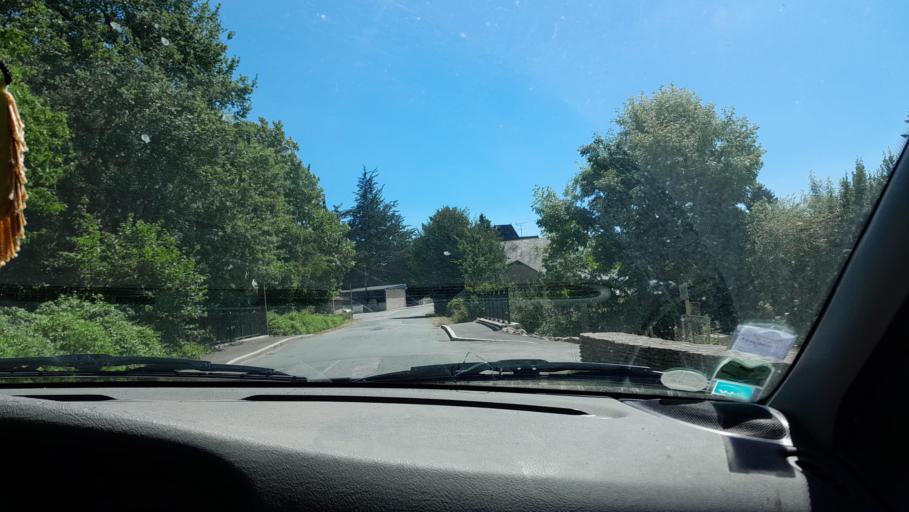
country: FR
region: Pays de la Loire
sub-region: Departement de Maine-et-Loire
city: Pouance
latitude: 47.8008
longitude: -1.2021
